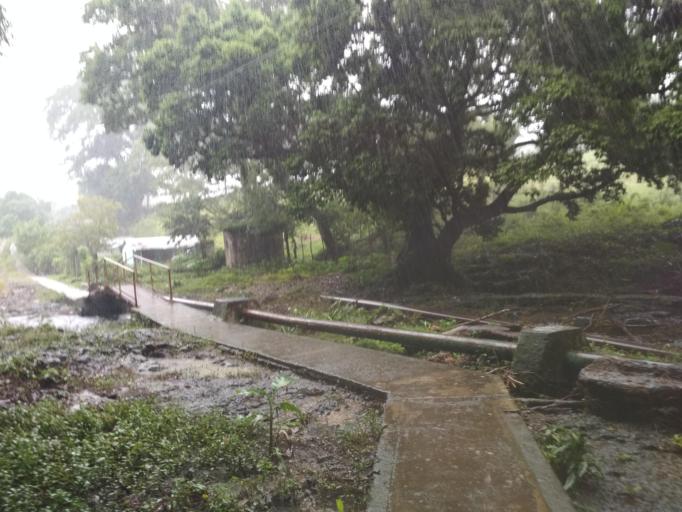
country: MX
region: Veracruz
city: Santiago Tuxtla
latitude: 18.4787
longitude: -95.2954
